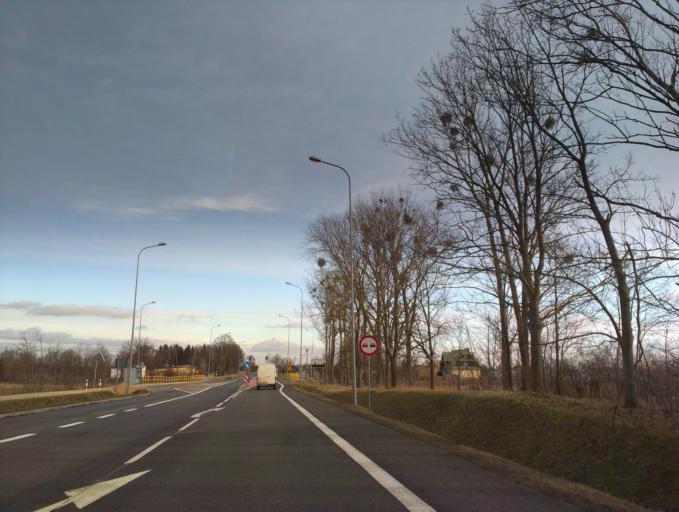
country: PL
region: Kujawsko-Pomorskie
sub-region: Powiat torunski
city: Czernikowo
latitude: 52.9333
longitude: 19.0101
